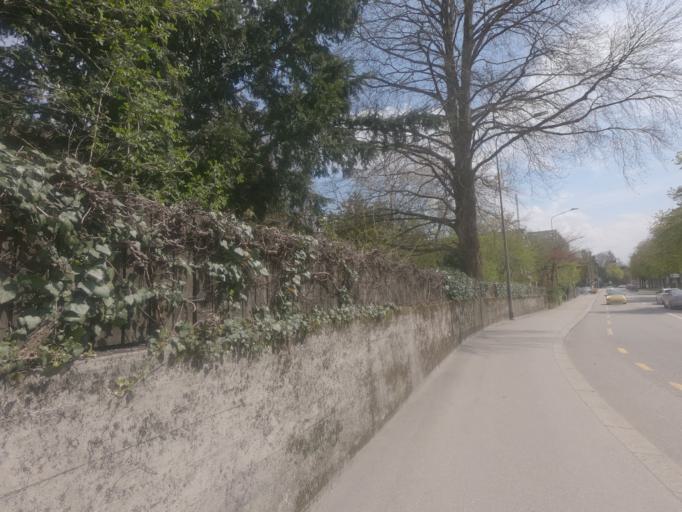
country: CH
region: Solothurn
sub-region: Bezirk Solothurn
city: Solothurn
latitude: 47.2112
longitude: 7.5398
